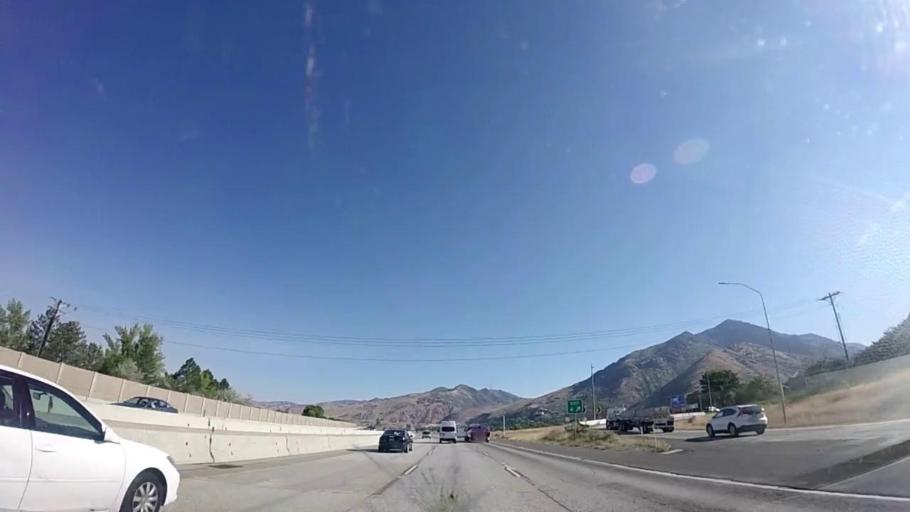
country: US
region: Utah
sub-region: Salt Lake County
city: Mount Olympus
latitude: 40.6817
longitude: -111.7978
